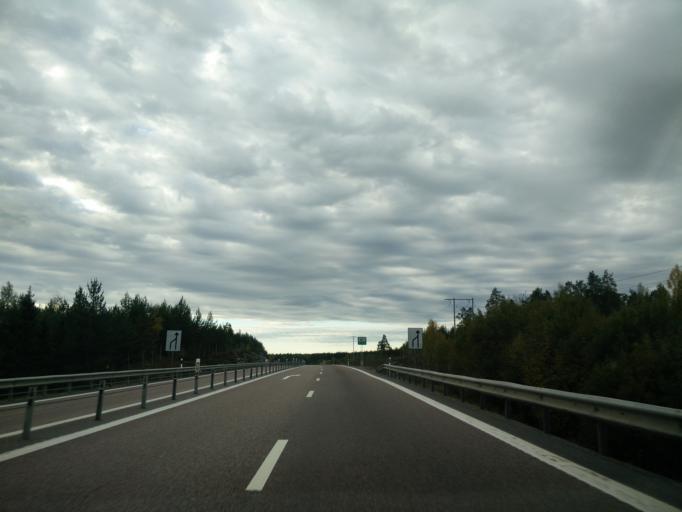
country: SE
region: Gaevleborg
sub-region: Hudiksvalls Kommun
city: Hudiksvall
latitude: 61.7336
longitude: 17.0669
